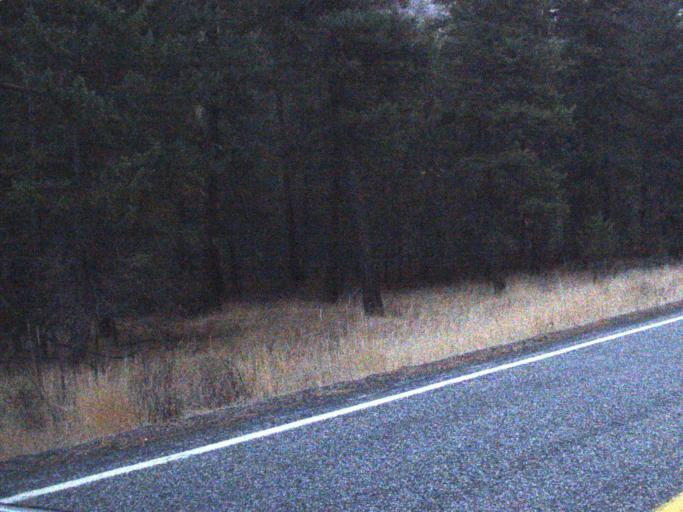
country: US
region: Washington
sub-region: Ferry County
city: Republic
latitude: 48.3613
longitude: -118.7410
